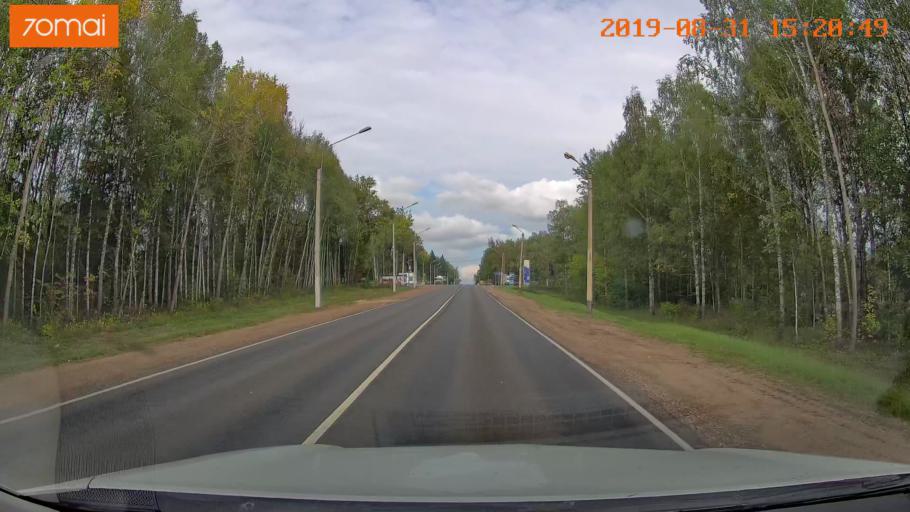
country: RU
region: Kaluga
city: Baryatino
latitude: 54.4924
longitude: 34.4428
